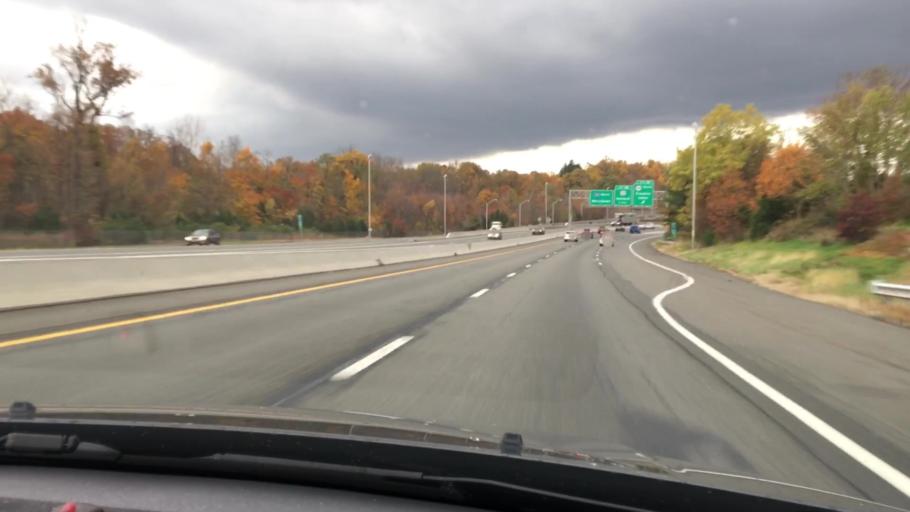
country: US
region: New Jersey
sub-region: Bergen County
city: Franklin Lakes
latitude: 41.0210
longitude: -74.2151
